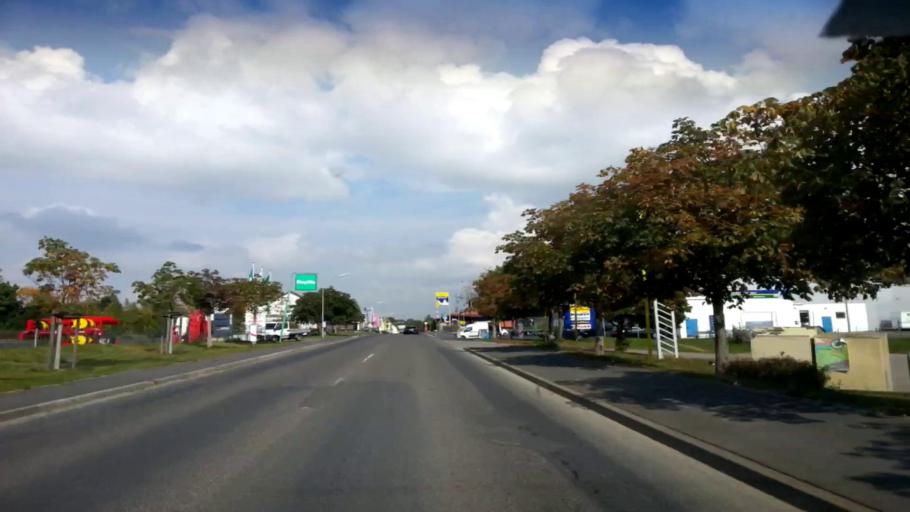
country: DE
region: Bavaria
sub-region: Regierungsbezirk Unterfranken
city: Wiesentheid
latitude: 49.7876
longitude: 10.3406
